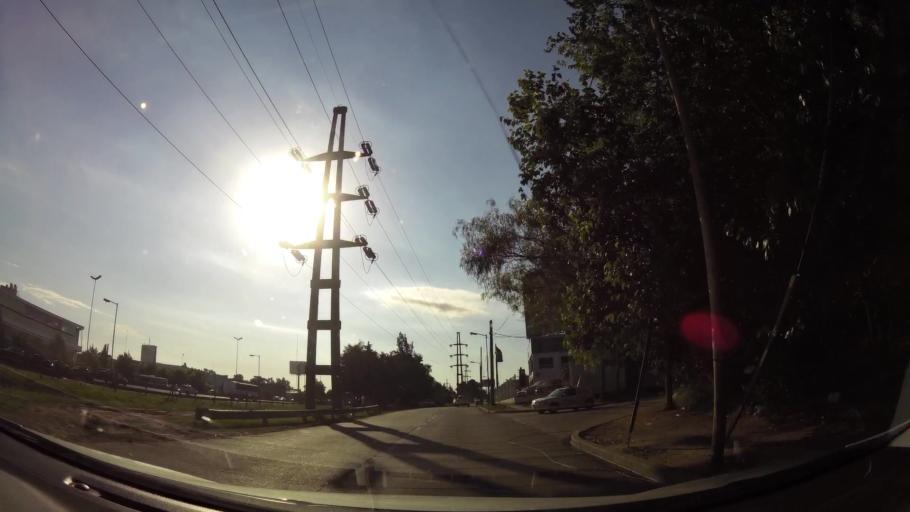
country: AR
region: Buenos Aires
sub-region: Partido de Tigre
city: Tigre
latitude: -34.4789
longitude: -58.6481
